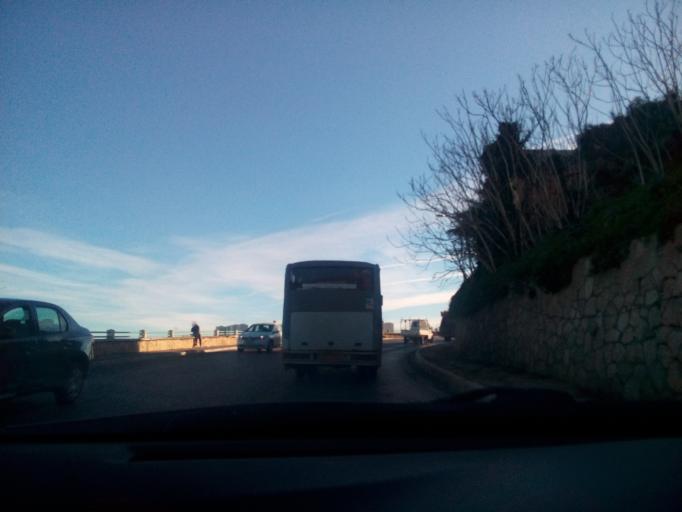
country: DZ
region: Oran
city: Oran
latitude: 35.7083
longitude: -0.6455
